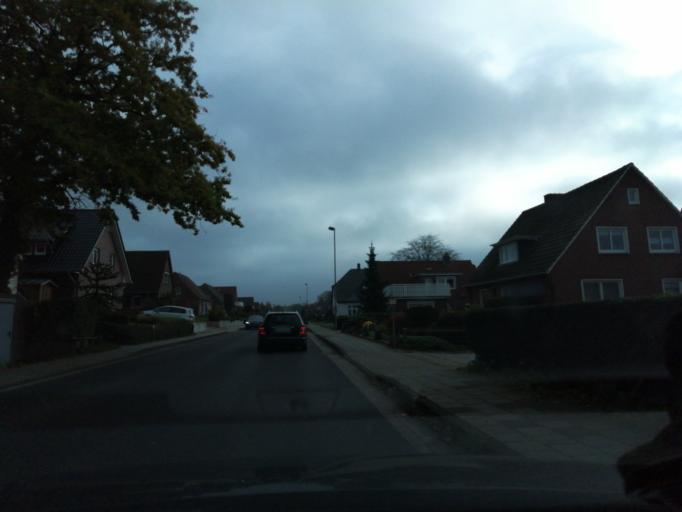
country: DE
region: Lower Saxony
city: Werdum
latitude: 53.6912
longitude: 7.8104
